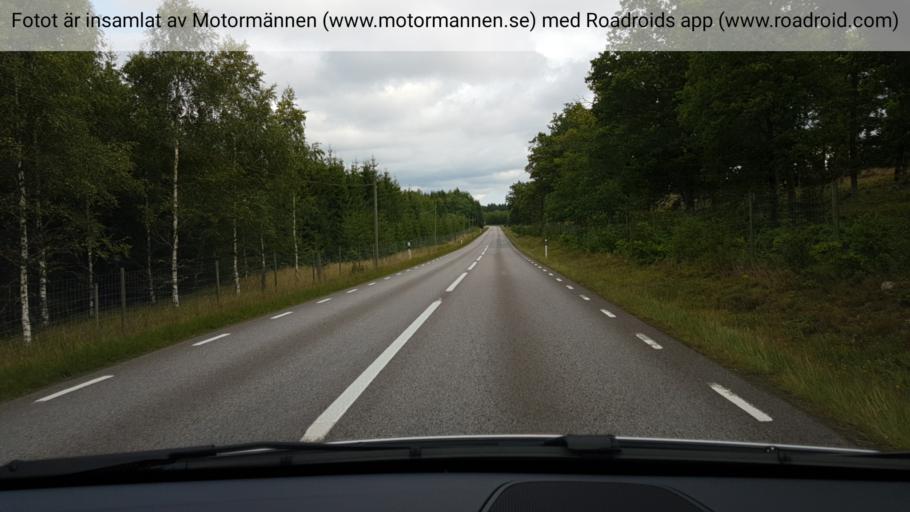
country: SE
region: Vaestra Goetaland
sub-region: Alingsas Kommun
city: Sollebrunn
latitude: 58.1767
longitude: 12.4179
